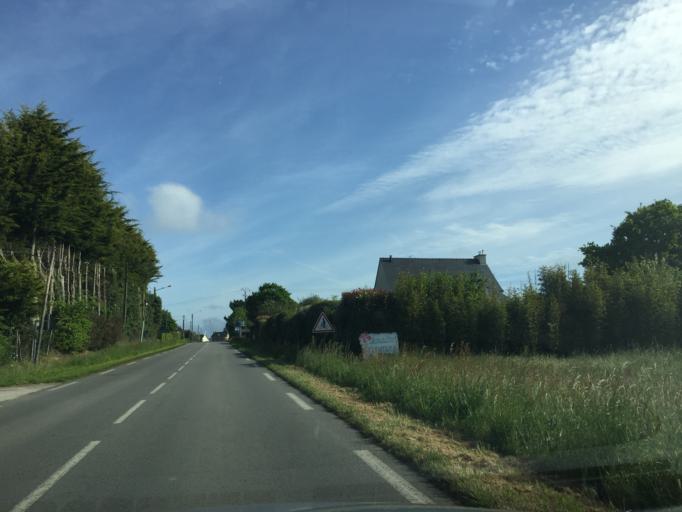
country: FR
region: Brittany
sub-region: Departement des Cotes-d'Armor
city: Crehen
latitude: 48.5792
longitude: -2.2348
